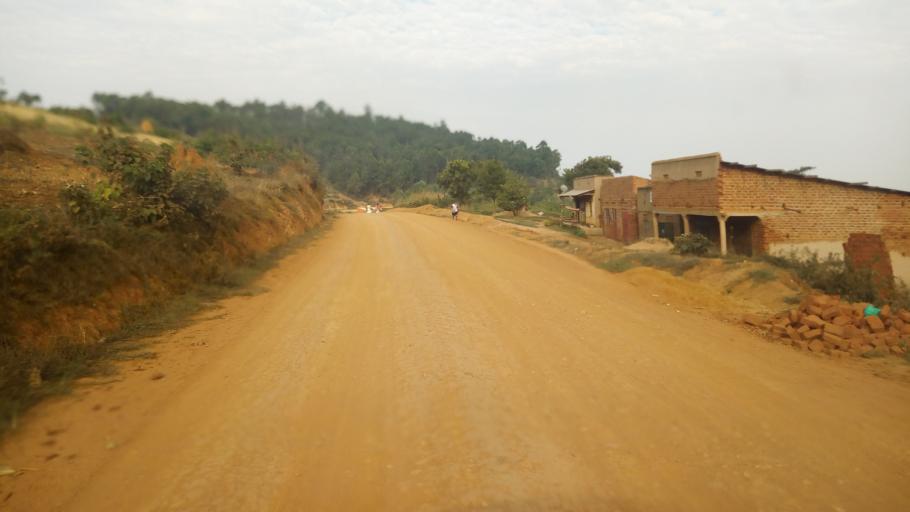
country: UG
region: Western Region
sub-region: Kanungu District
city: Ntungamo
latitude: -0.8304
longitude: 29.6978
